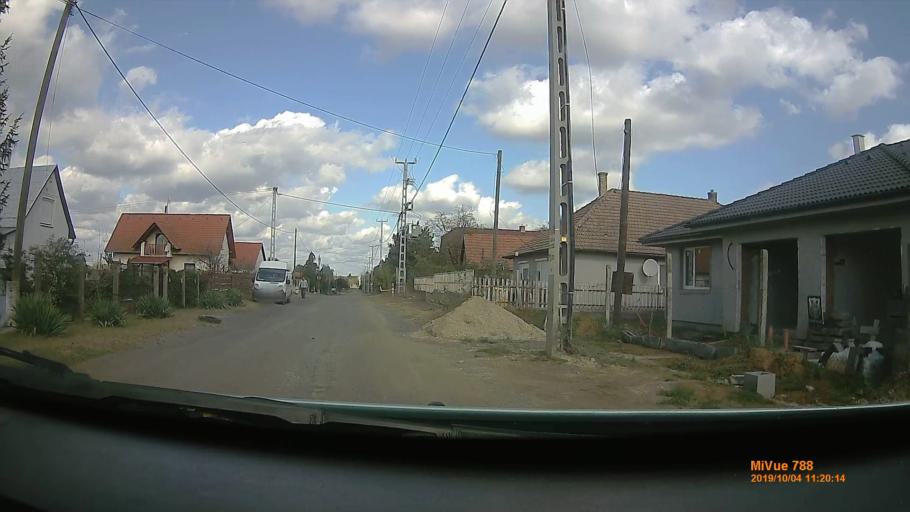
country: HU
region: Szabolcs-Szatmar-Bereg
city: Nyirtelek
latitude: 47.9918
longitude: 21.6758
